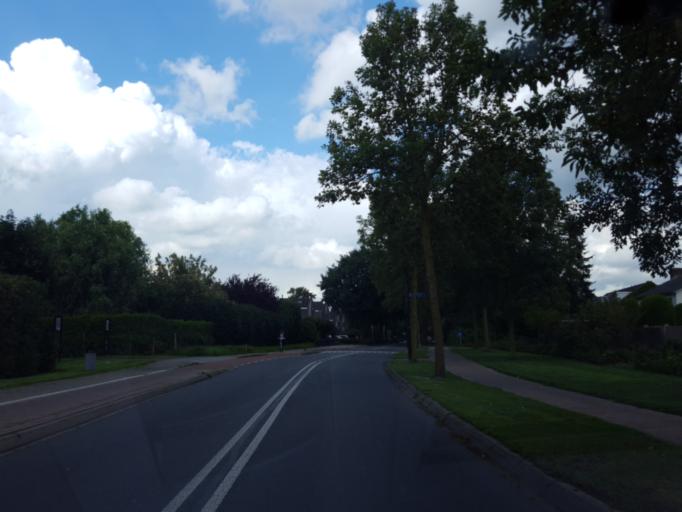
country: NL
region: Gelderland
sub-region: Gemeente Beuningen
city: Beuningen
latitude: 51.8549
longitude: 5.7644
